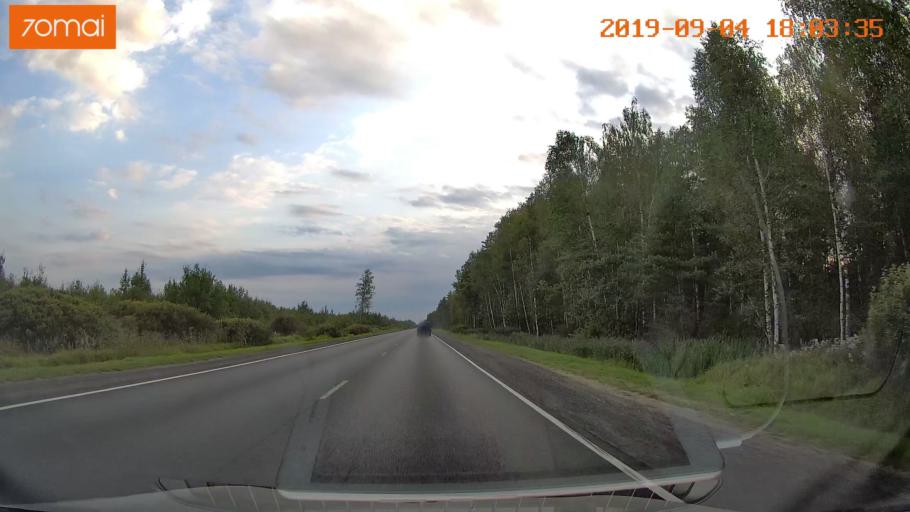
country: RU
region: Moskovskaya
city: Il'inskiy Pogost
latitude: 55.4618
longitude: 38.8502
